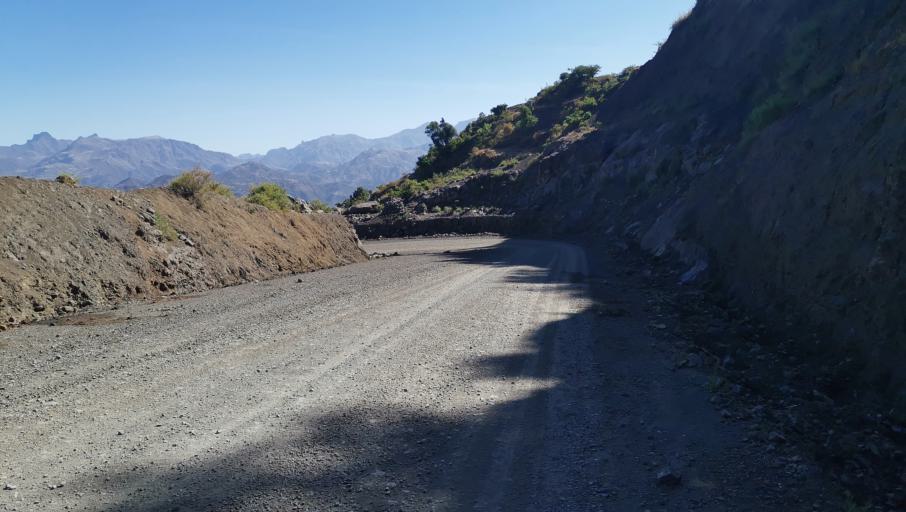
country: ET
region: Amhara
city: Lalibela
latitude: 12.2080
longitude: 39.0052
